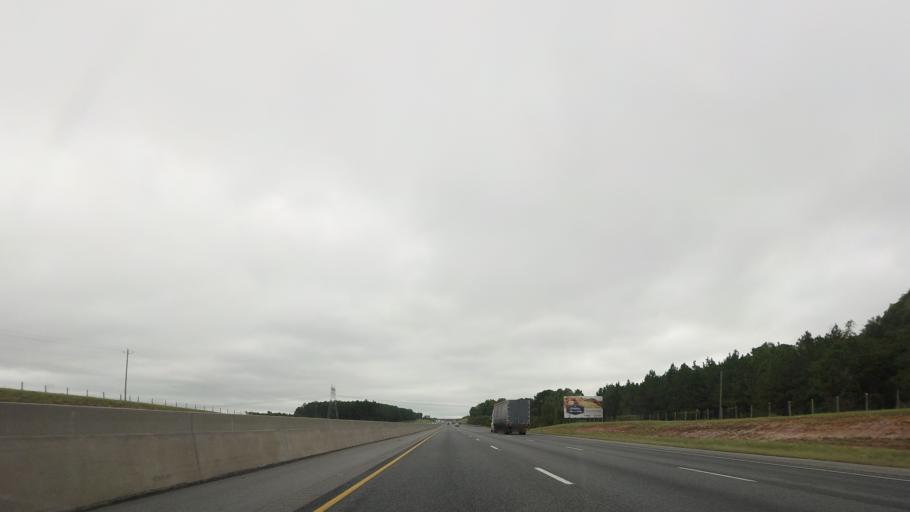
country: US
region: Georgia
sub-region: Tift County
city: Tifton
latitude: 31.5404
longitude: -83.5292
